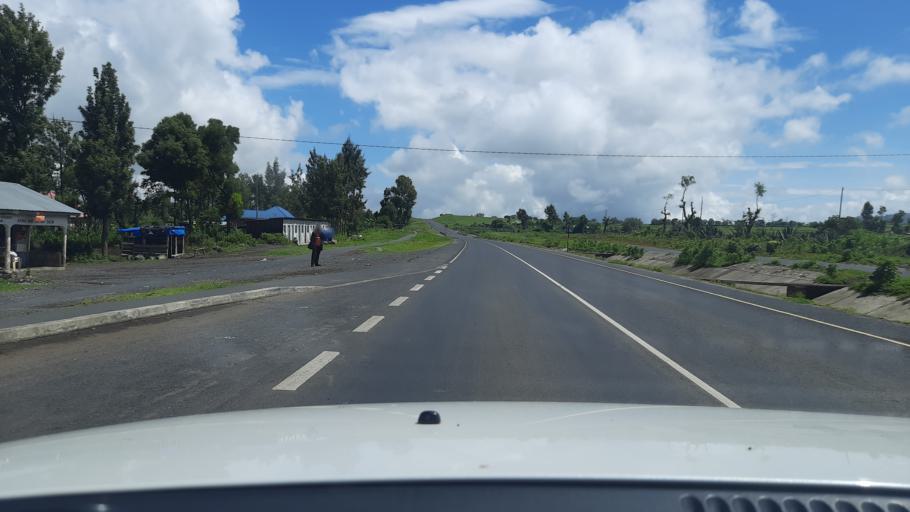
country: TZ
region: Arusha
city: Arusha
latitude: -3.1801
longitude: 36.6728
